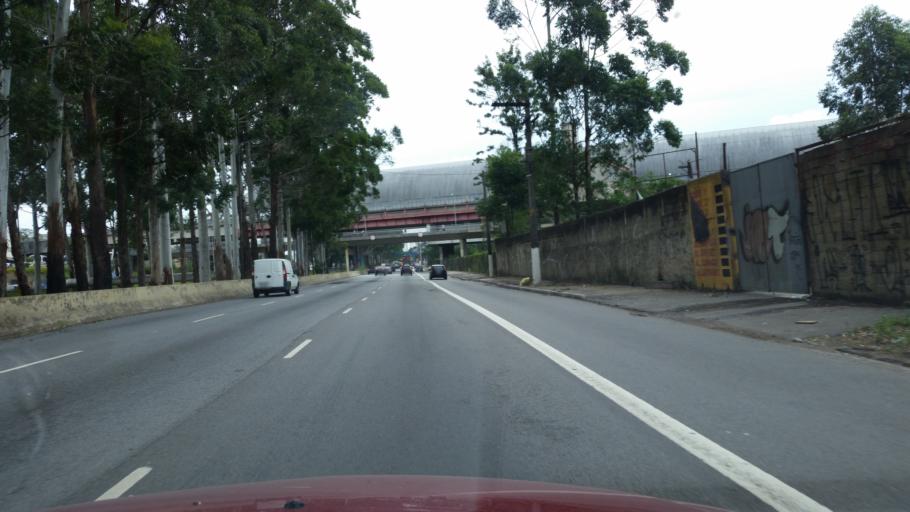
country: BR
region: Sao Paulo
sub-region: Ferraz De Vasconcelos
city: Ferraz de Vasconcelos
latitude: -23.5433
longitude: -46.4478
